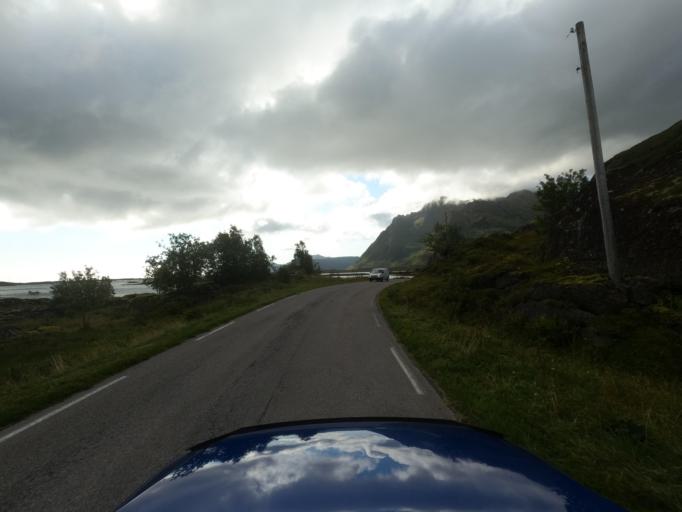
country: NO
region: Nordland
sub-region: Vestvagoy
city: Evjen
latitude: 68.1966
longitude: 13.8820
